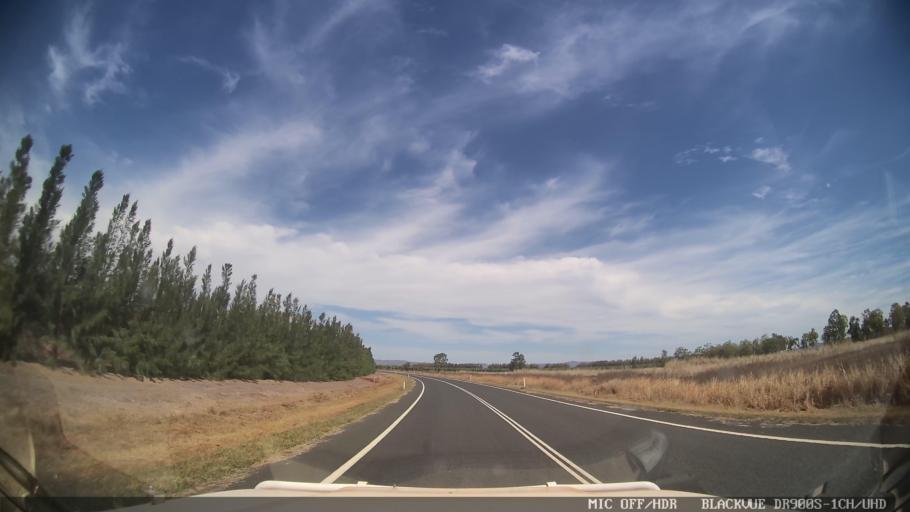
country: AU
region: Queensland
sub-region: Cook
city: Cooktown
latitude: -15.8334
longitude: 144.8555
